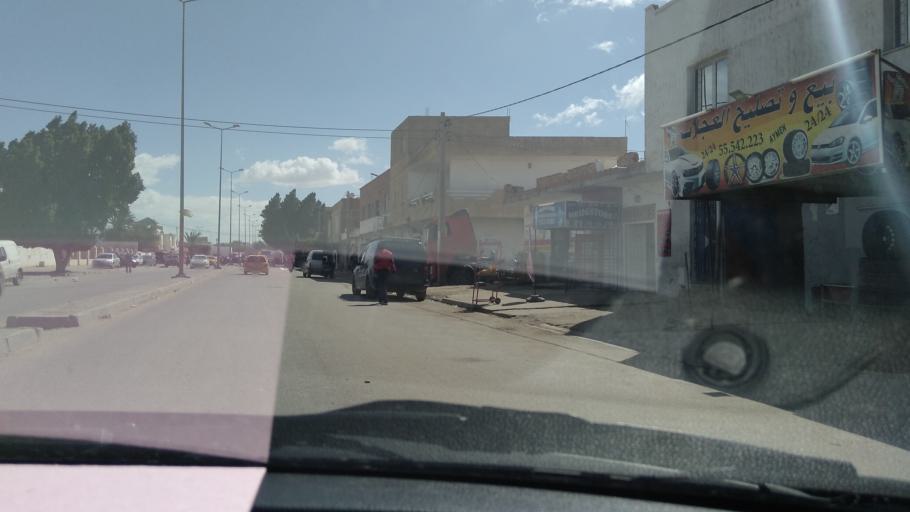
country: TN
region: Al Qayrawan
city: Kairouan
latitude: 35.6811
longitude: 10.0839
